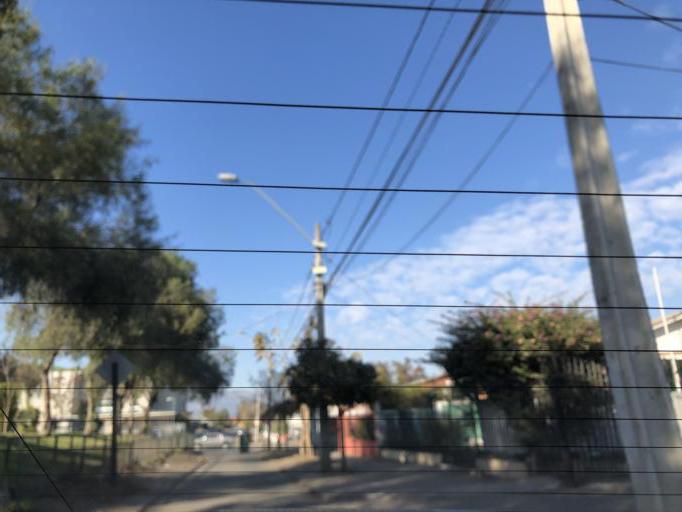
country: CL
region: Santiago Metropolitan
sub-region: Provincia de Cordillera
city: Puente Alto
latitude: -33.6177
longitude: -70.5879
